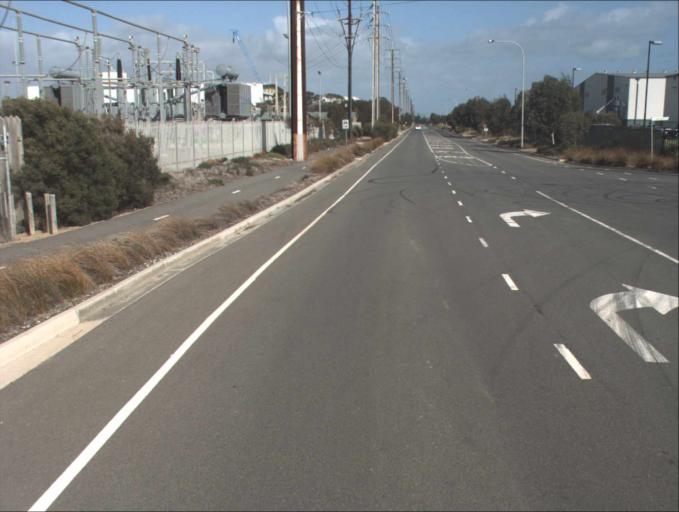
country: AU
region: South Australia
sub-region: Port Adelaide Enfield
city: Birkenhead
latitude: -34.7789
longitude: 138.5087
